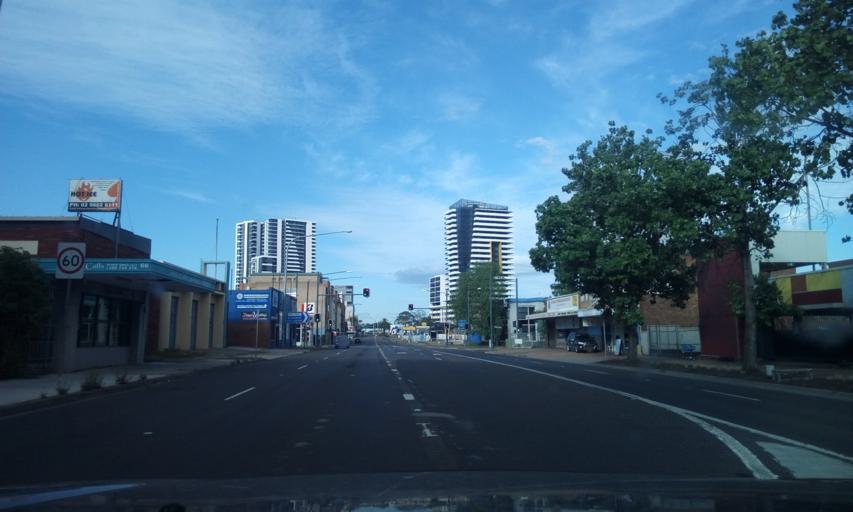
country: AU
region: New South Wales
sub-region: Fairfield
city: Liverpool
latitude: -33.9257
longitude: 150.9240
